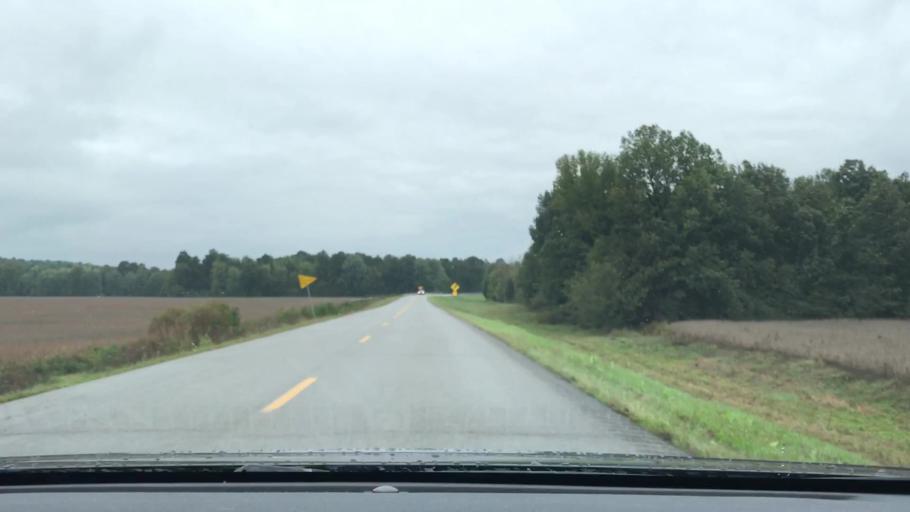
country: US
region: Kentucky
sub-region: McLean County
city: Calhoun
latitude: 37.4938
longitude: -87.2459
